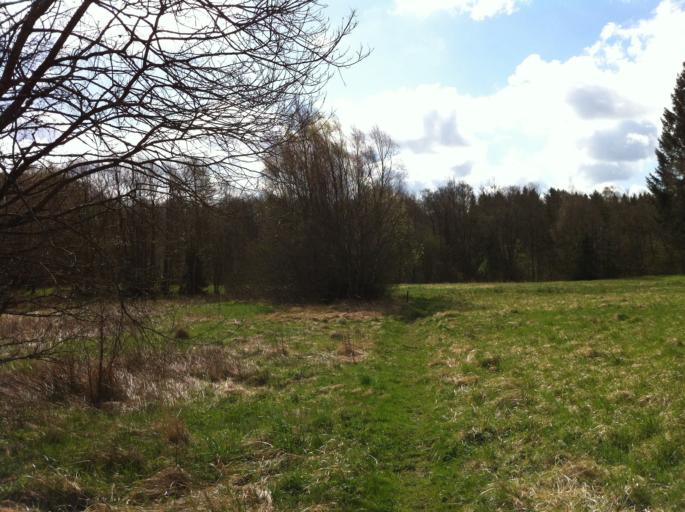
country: SE
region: Skane
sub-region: Horby Kommun
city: Hoerby
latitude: 55.9197
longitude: 13.6304
